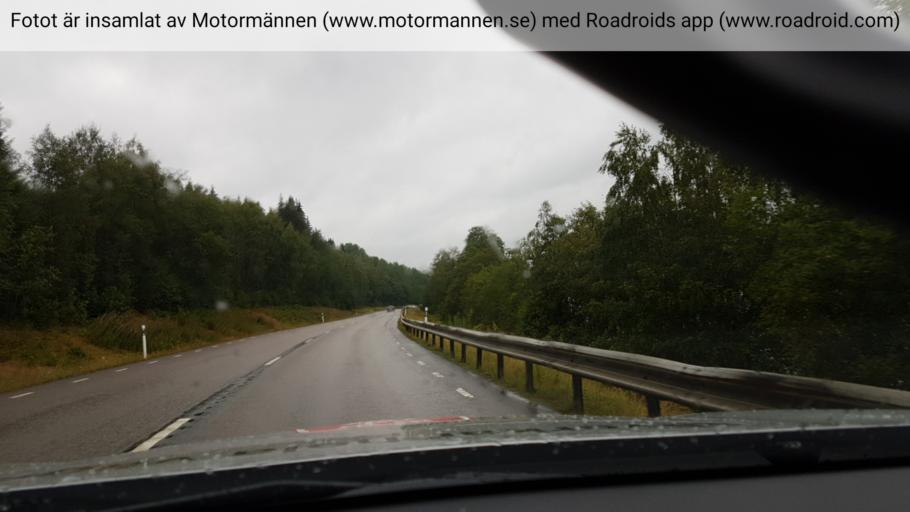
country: SE
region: Vaestra Goetaland
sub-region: Bengtsfors Kommun
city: Billingsfors
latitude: 58.9389
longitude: 12.0951
